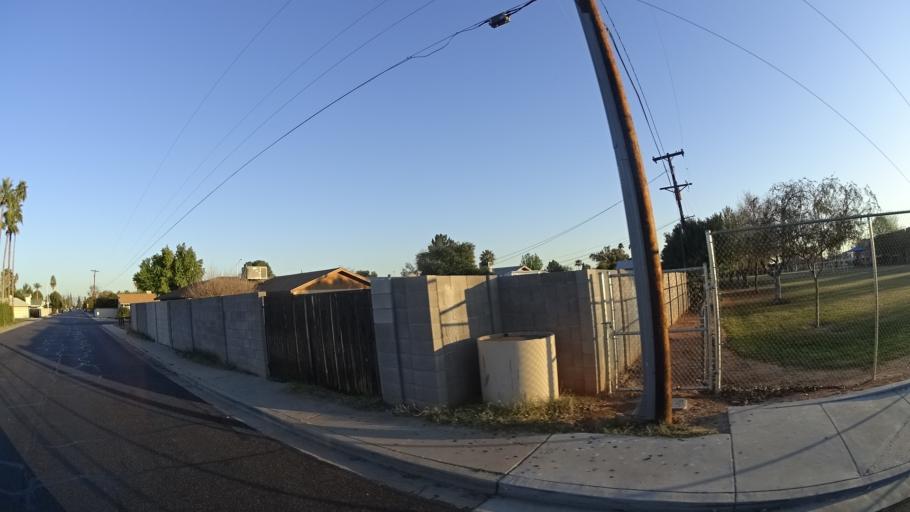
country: US
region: Arizona
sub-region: Maricopa County
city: Mesa
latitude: 33.4260
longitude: -111.8120
